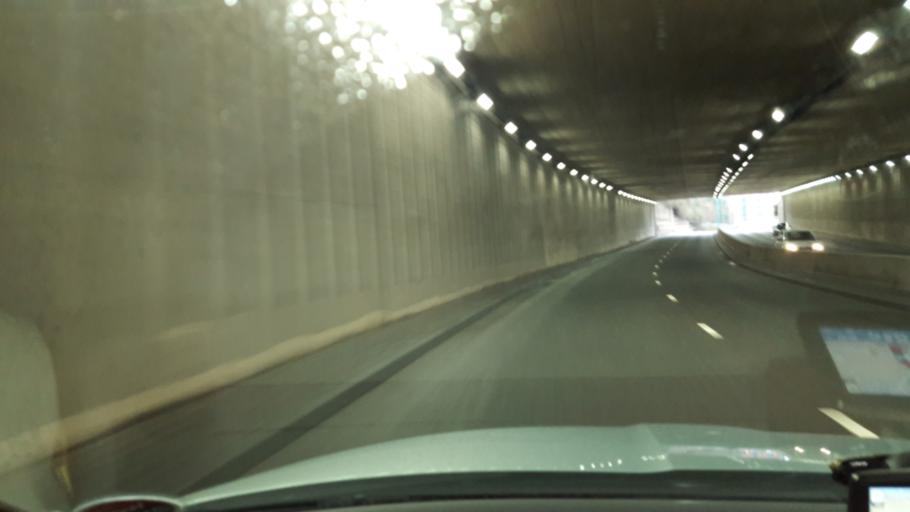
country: GB
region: Scotland
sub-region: Dundee City
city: Dundee
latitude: 56.4652
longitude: -2.9712
